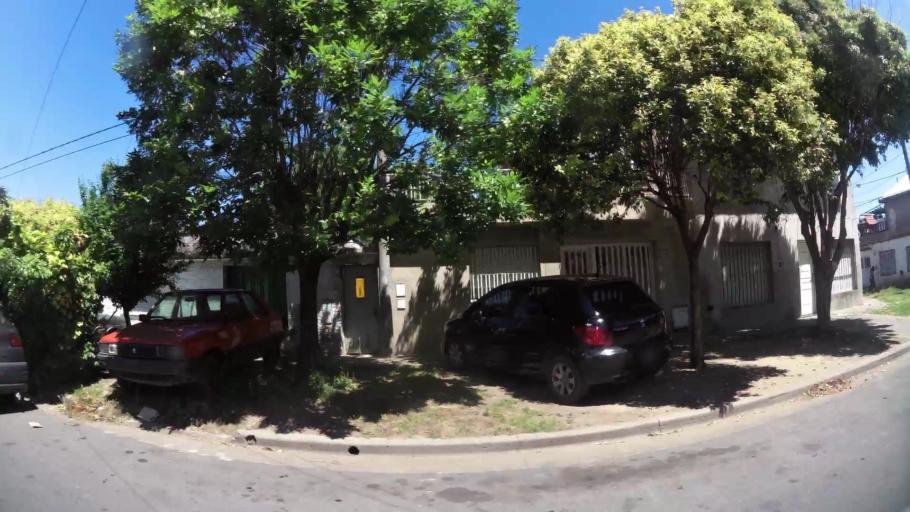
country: AR
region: Santa Fe
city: Perez
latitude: -32.9465
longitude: -60.7159
